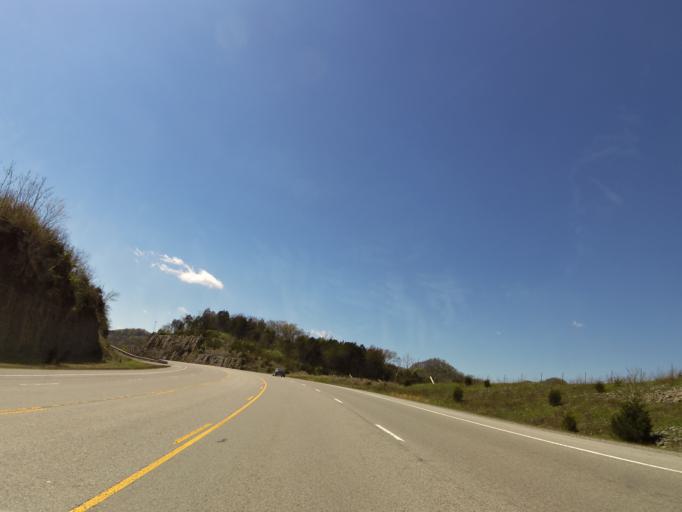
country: US
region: Tennessee
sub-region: DeKalb County
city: Smithville
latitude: 36.0150
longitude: -85.9546
